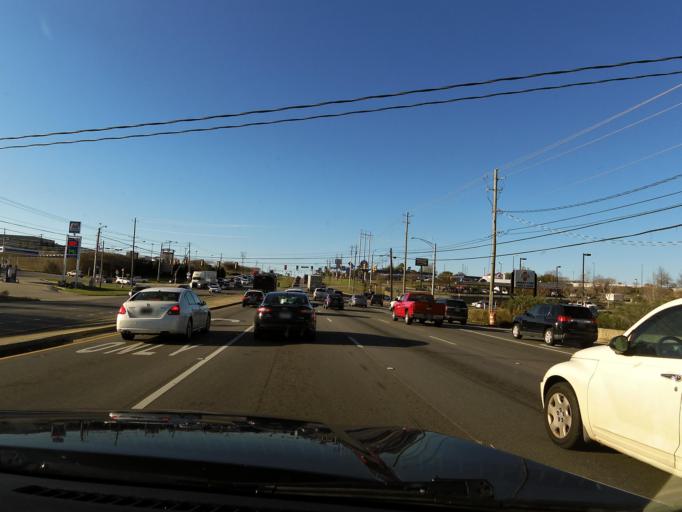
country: US
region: Alabama
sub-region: Houston County
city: Dothan
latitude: 31.2633
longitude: -85.4398
